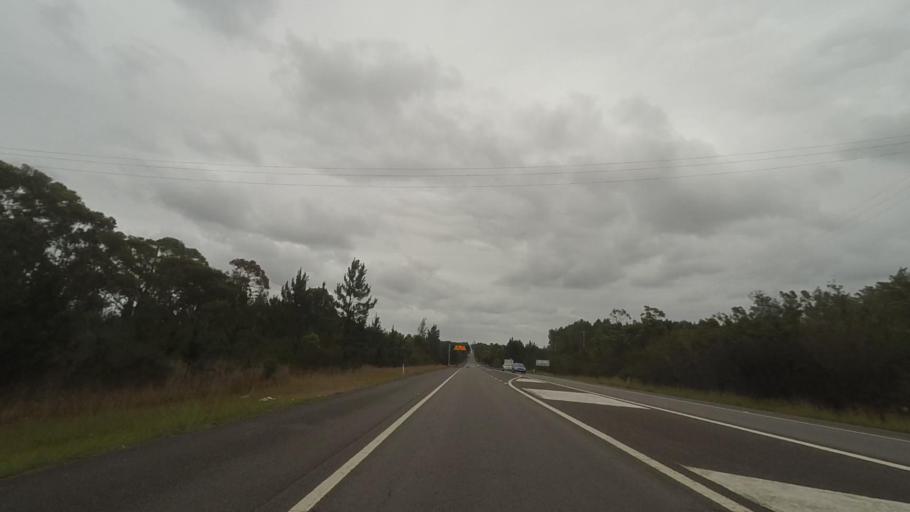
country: AU
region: New South Wales
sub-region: Wyong Shire
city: Charmhaven
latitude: -33.2063
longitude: 151.4965
